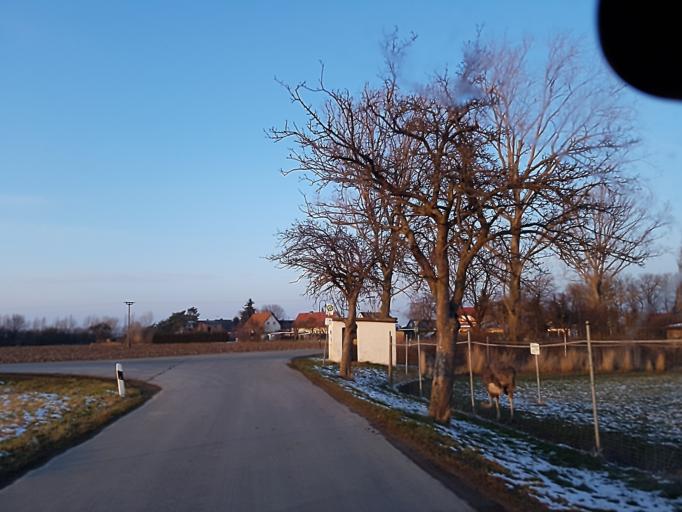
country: DE
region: Saxony
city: Strehla
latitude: 51.3906
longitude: 13.2250
